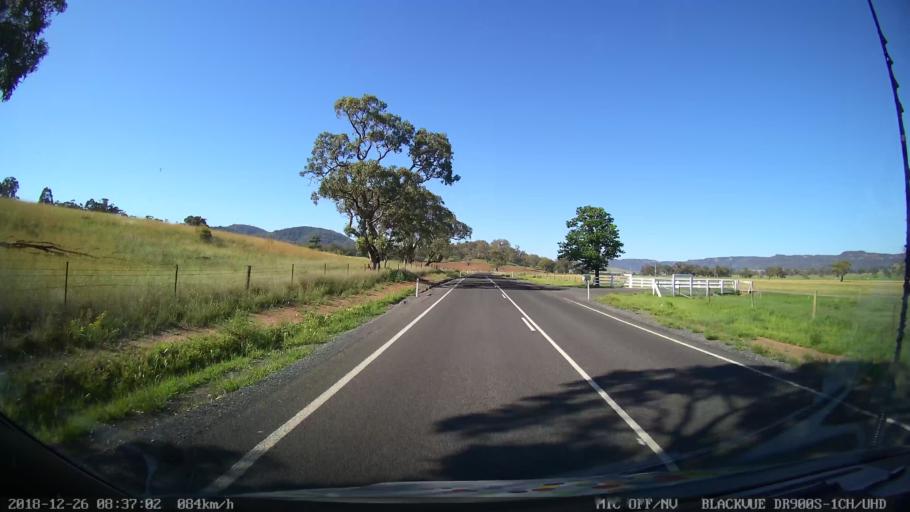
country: AU
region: New South Wales
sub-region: Upper Hunter Shire
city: Merriwa
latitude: -32.4282
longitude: 150.0937
